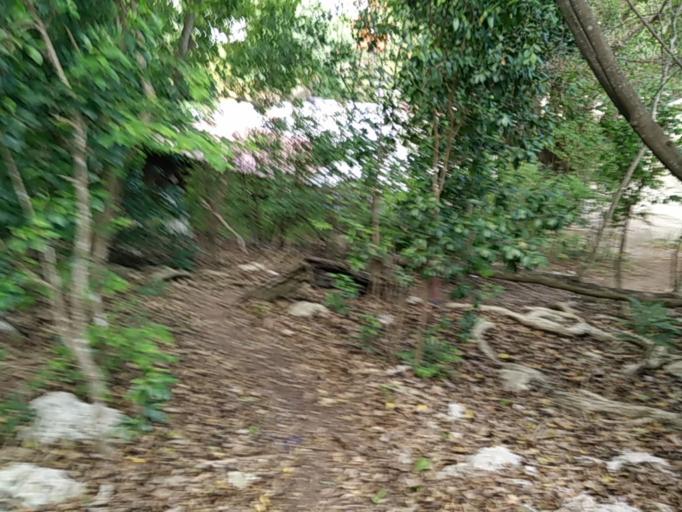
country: GP
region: Guadeloupe
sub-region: Guadeloupe
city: Sainte-Anne
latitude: 16.2101
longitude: -61.4261
